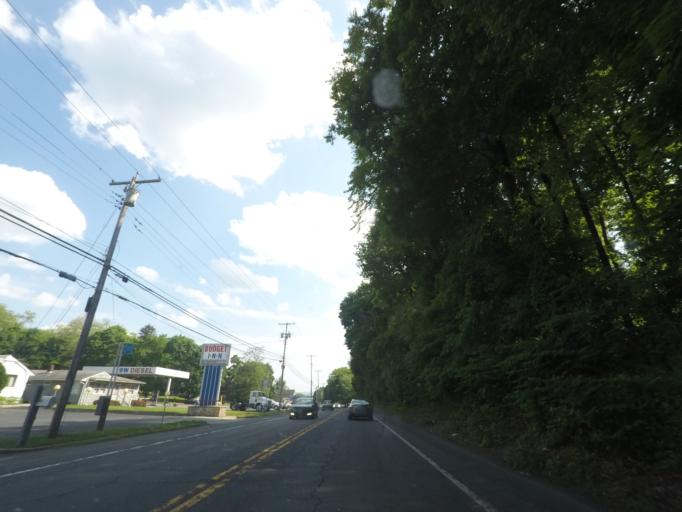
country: US
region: New York
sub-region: Orange County
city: Balmville
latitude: 41.5427
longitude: -74.0124
